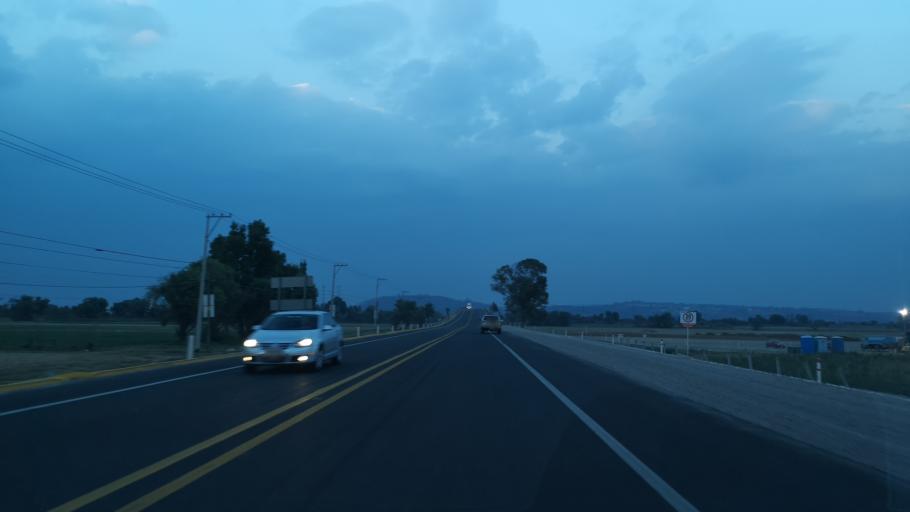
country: MX
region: Puebla
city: Santa Ana Xalmimilulco
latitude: 19.2030
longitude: -98.3626
